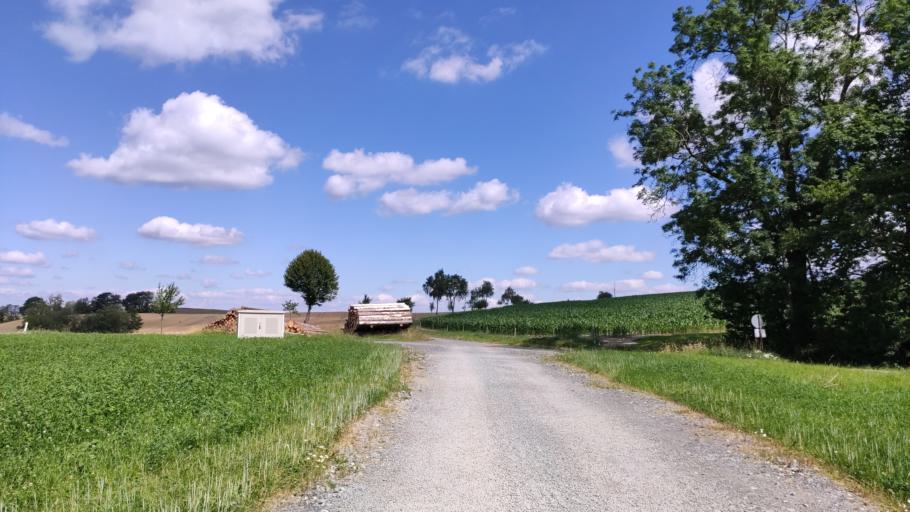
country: DE
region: Bavaria
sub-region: Upper Franconia
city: Ludwigsstadt
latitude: 50.5014
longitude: 11.4181
